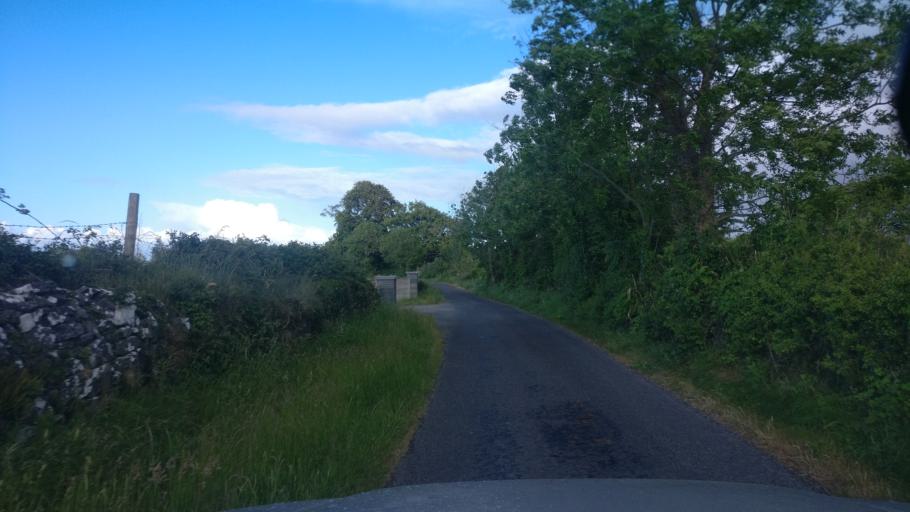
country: IE
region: Connaught
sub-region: County Galway
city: Ballinasloe
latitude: 53.2471
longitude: -8.2270
